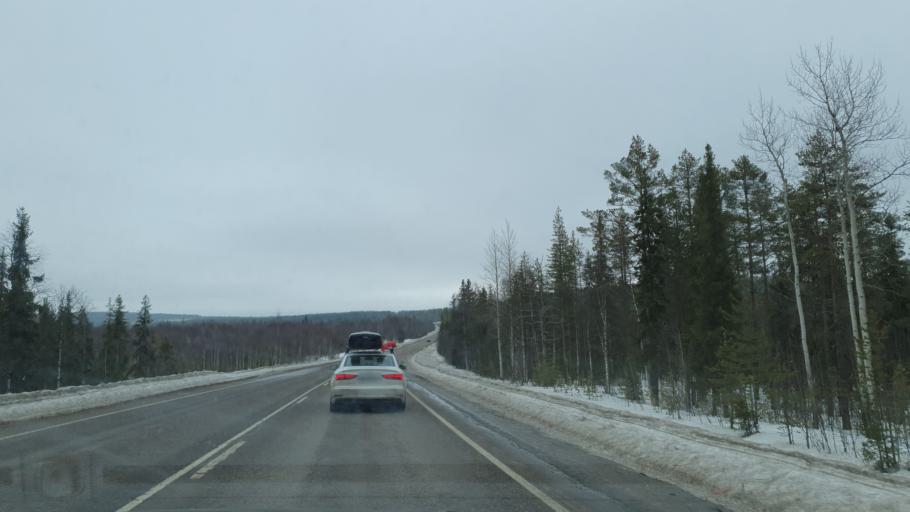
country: FI
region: Lapland
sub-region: Torniolaakso
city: Pello
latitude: 66.8699
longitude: 24.0529
